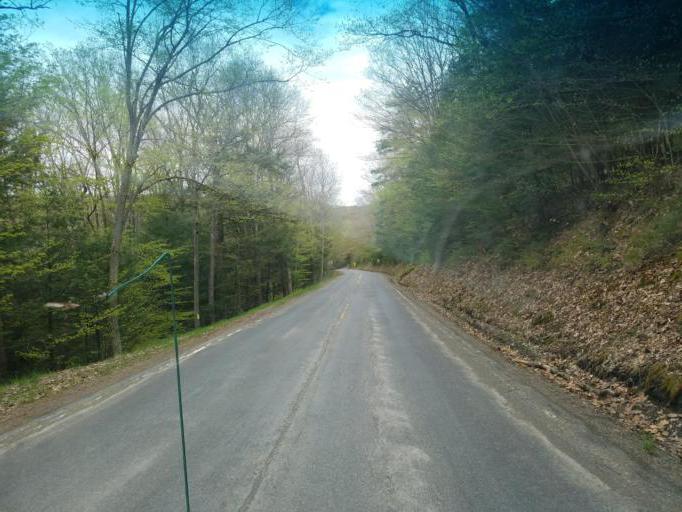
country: US
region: Pennsylvania
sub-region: Tioga County
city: Wellsboro
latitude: 41.6997
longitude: -77.4473
